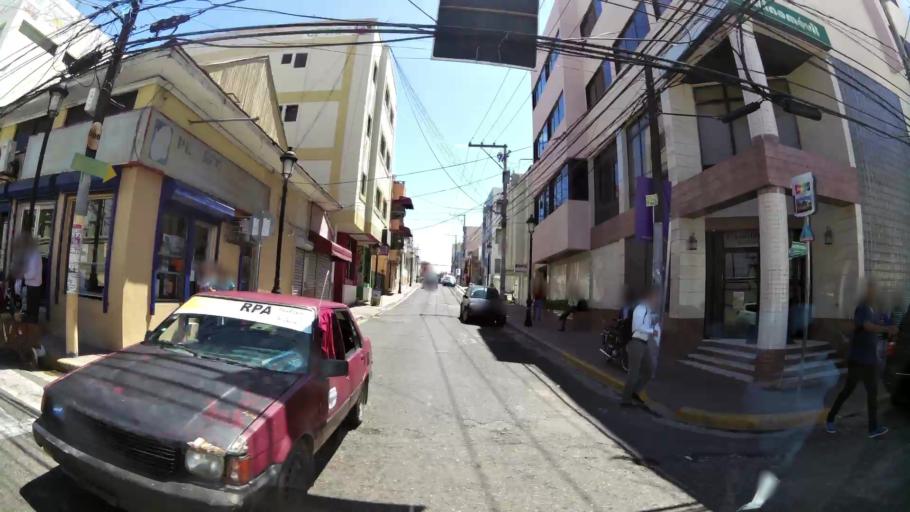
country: DO
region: Santiago
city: Santiago de los Caballeros
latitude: 19.4524
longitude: -70.7018
